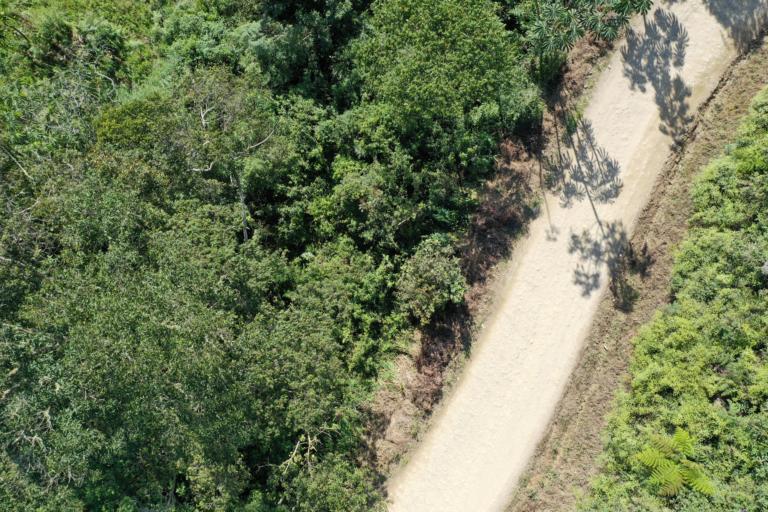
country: BO
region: La Paz
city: Coroico
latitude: -16.2546
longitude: -67.6985
